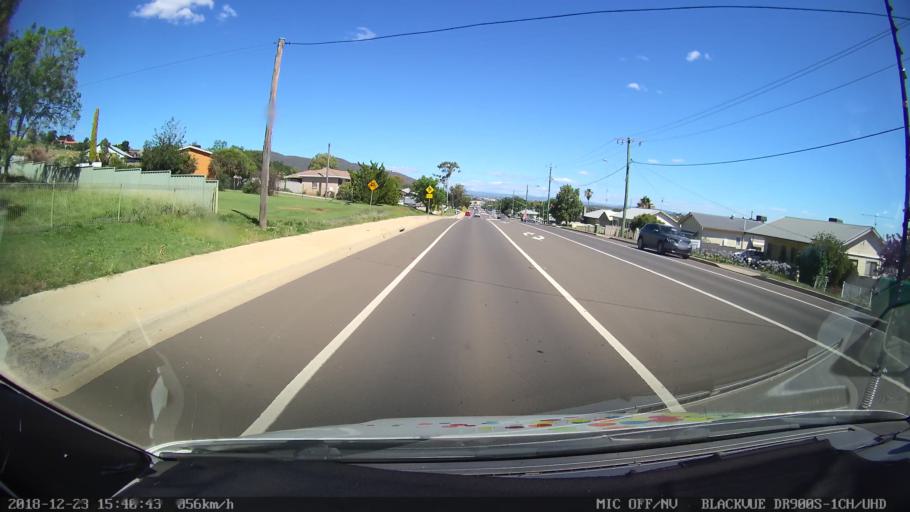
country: AU
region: New South Wales
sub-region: Tamworth Municipality
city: Tamworth
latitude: -31.0725
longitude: 150.9119
